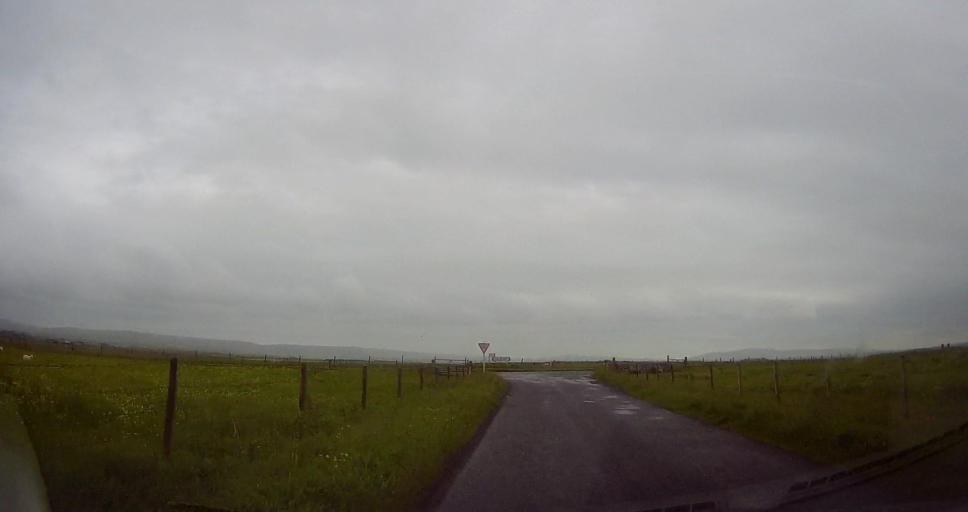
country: GB
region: Scotland
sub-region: Orkney Islands
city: Stromness
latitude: 59.0688
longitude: -3.2815
